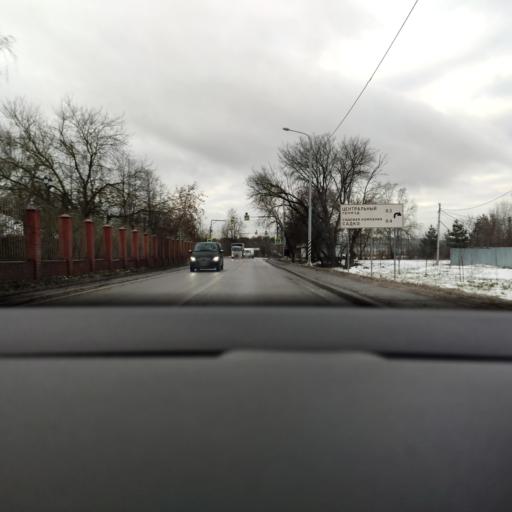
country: RU
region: Moskovskaya
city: Lesnyye Polyany
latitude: 55.9605
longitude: 37.8459
